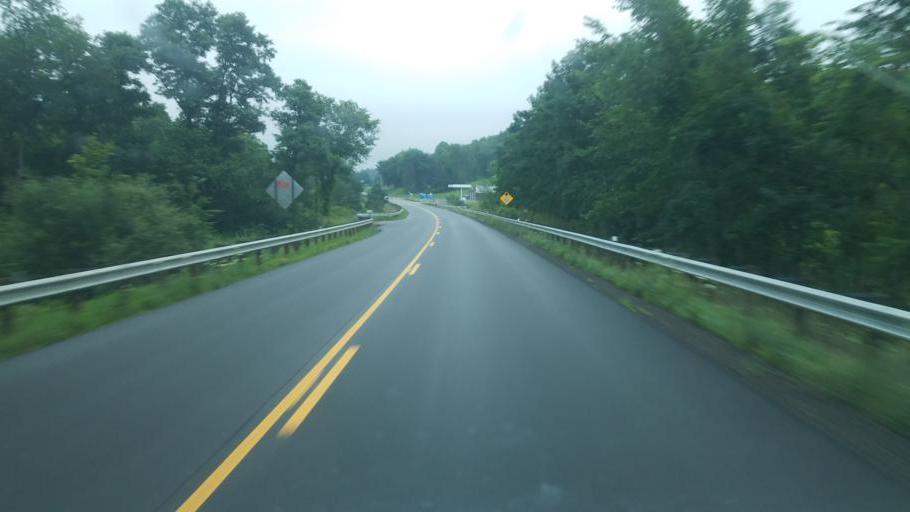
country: US
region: Ohio
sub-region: Tuscarawas County
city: Rockford
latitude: 40.4251
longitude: -81.1993
